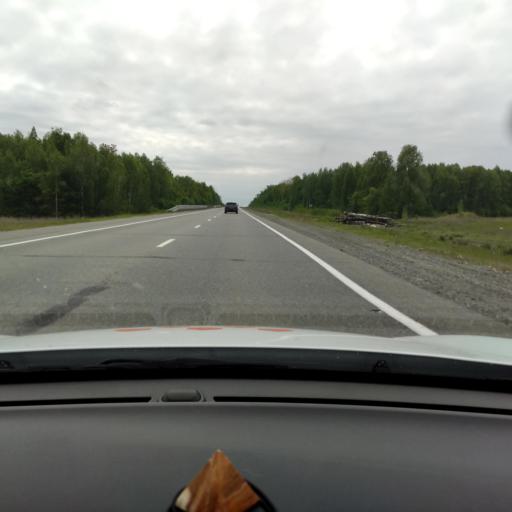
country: RU
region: Tatarstan
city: Pestretsy
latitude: 55.5987
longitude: 49.7090
